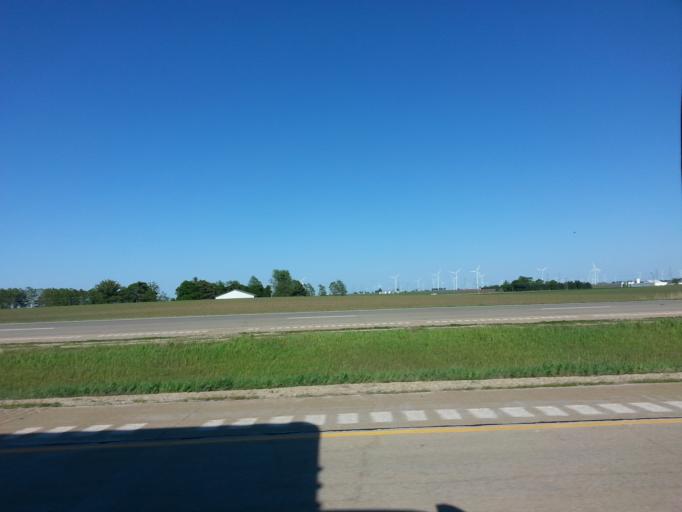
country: US
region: Illinois
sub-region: Woodford County
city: Minonk
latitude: 40.8847
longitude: -89.0369
